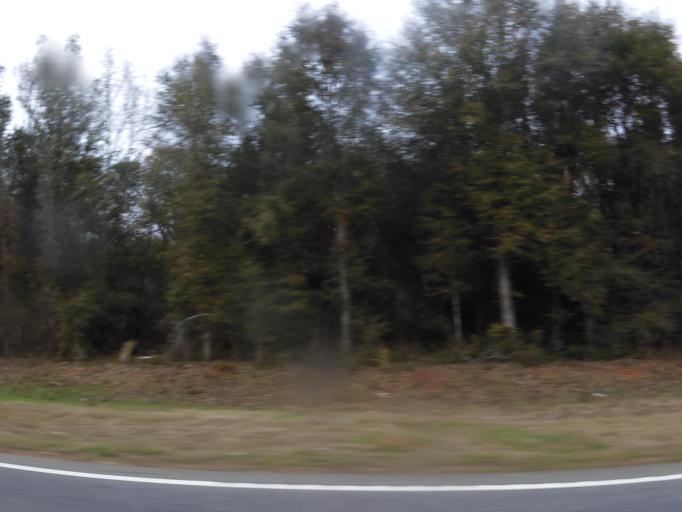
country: US
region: Georgia
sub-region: Randolph County
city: Shellman
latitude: 31.7702
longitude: -84.5575
